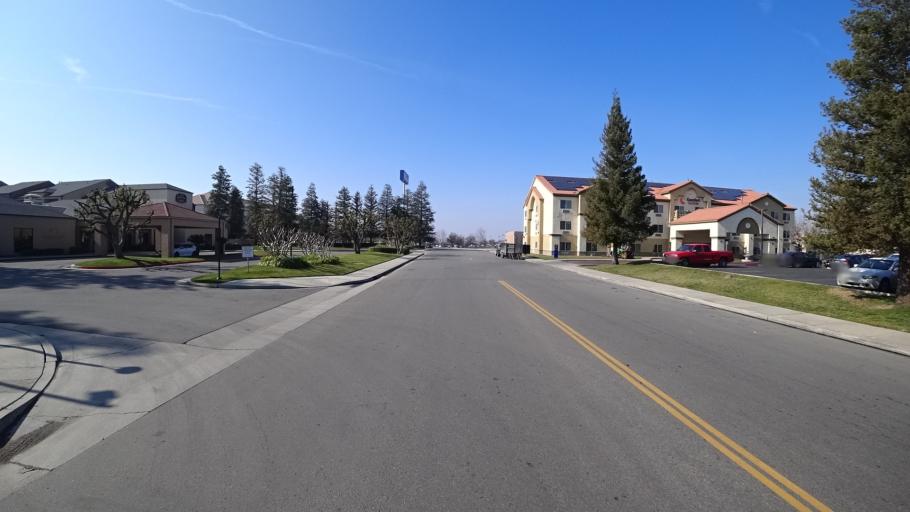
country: US
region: California
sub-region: Kern County
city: Bakersfield
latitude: 35.3808
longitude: -119.0471
